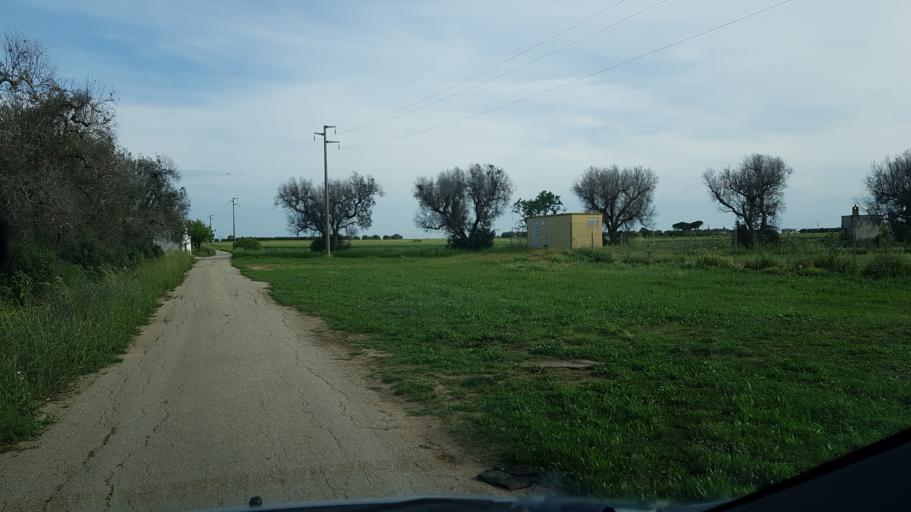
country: IT
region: Apulia
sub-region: Provincia di Brindisi
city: Tuturano
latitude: 40.5139
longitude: 17.9602
